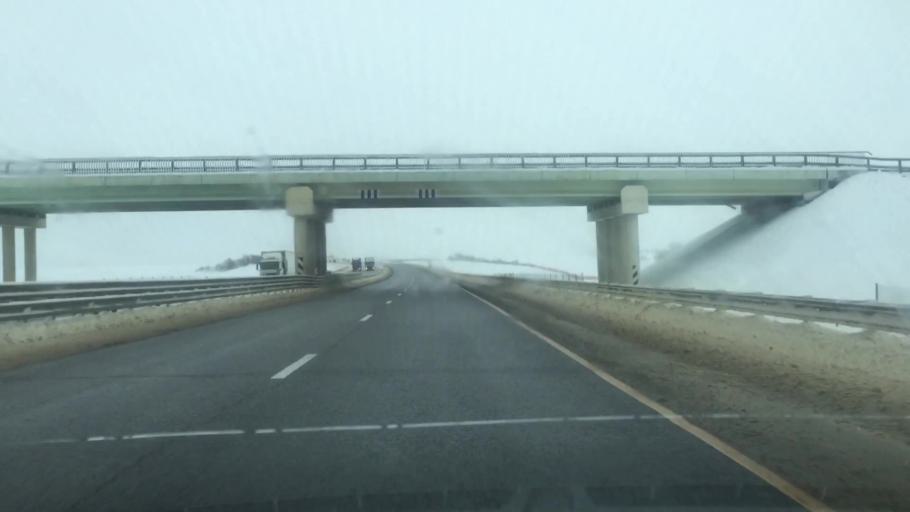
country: RU
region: Tula
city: Yefremov
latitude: 53.2252
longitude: 38.2085
